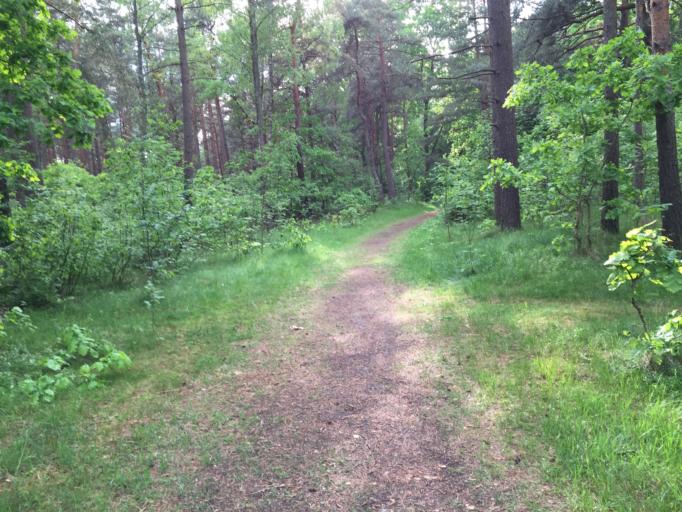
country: LT
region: Klaipedos apskritis
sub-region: Klaipeda
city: Klaipeda
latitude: 55.7476
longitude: 21.1235
